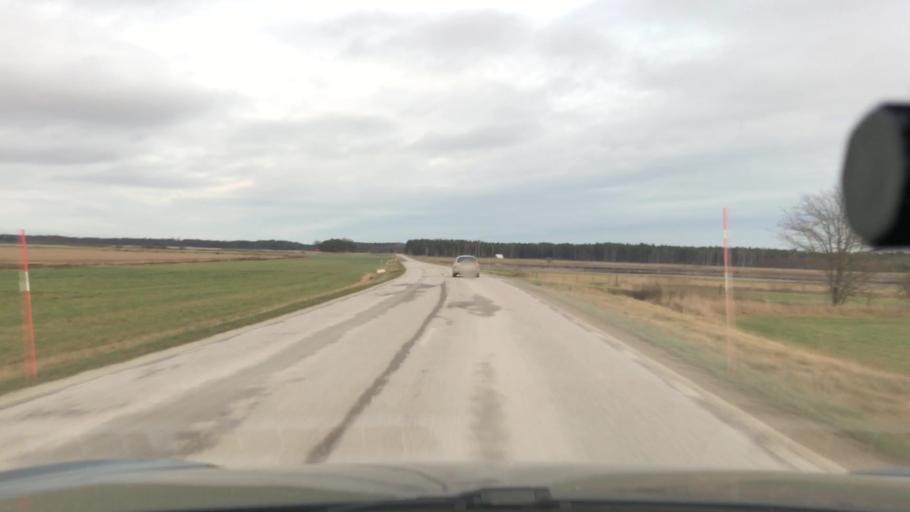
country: SE
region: Gotland
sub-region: Gotland
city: Visby
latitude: 57.7107
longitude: 18.5415
